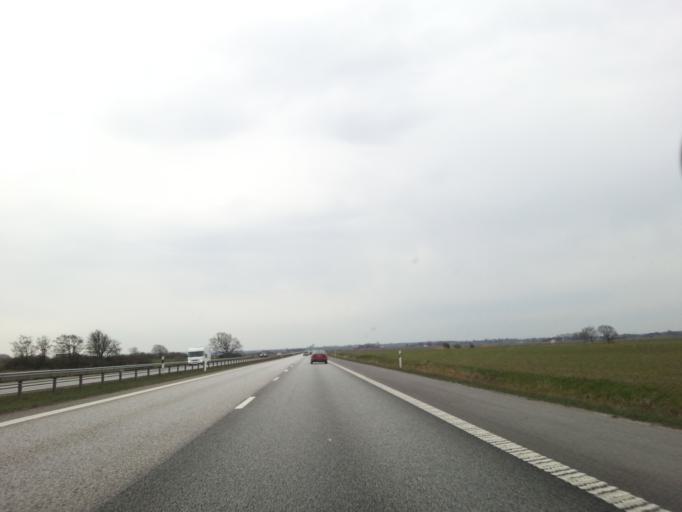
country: SE
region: Skane
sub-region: Angelholms Kommun
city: AEngelholm
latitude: 56.3012
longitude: 12.9064
